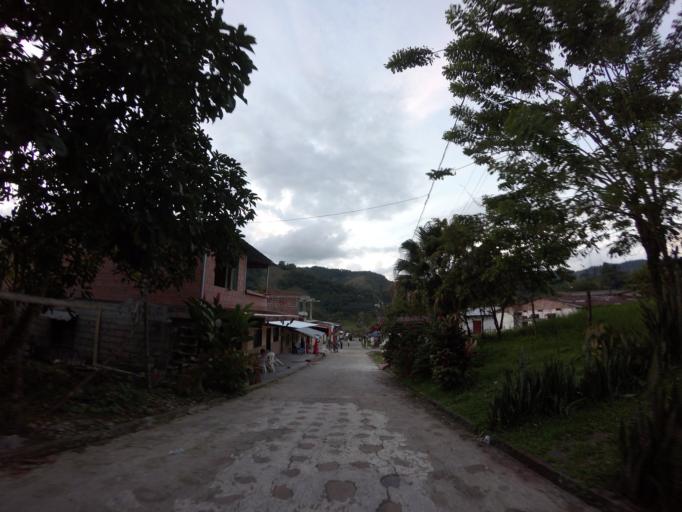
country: CO
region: Antioquia
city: Narino
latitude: 5.5331
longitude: -75.1325
